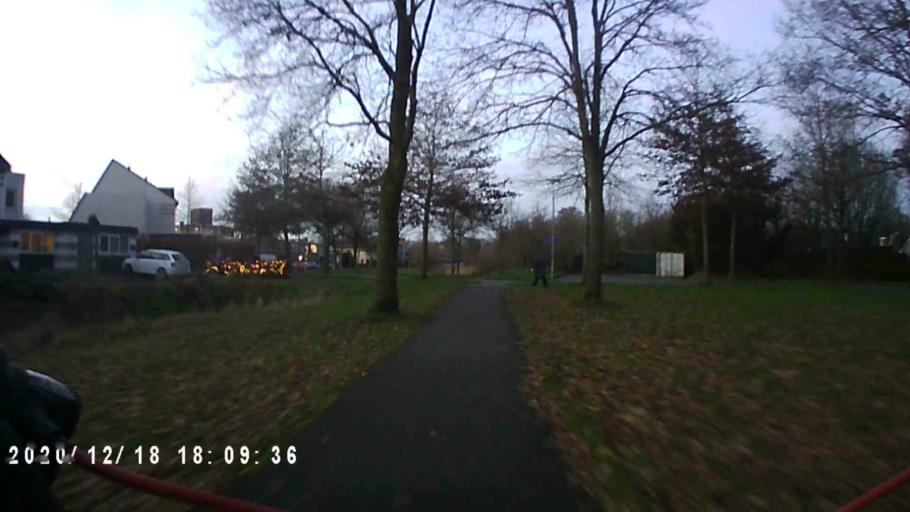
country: NL
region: Groningen
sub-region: Gemeente Haren
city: Haren
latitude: 53.1402
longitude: 6.5524
